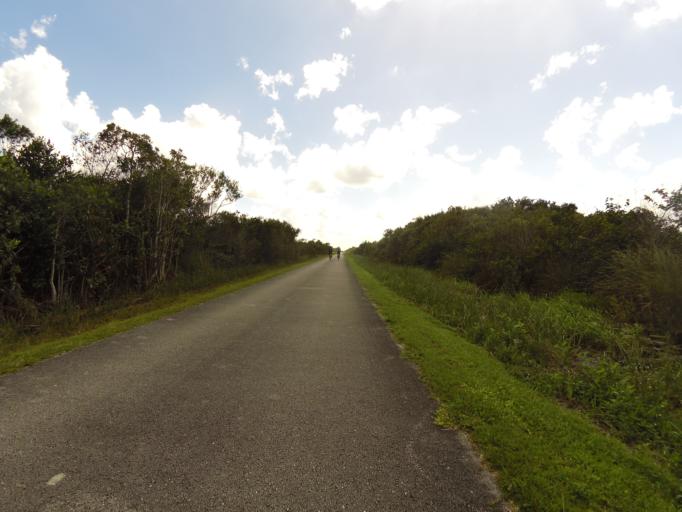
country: US
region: Florida
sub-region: Miami-Dade County
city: The Hammocks
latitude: 25.7142
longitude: -80.7668
